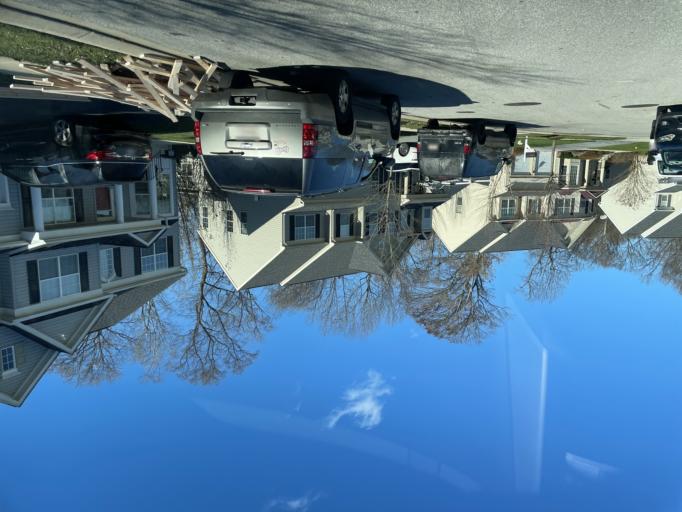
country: US
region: Maryland
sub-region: Baltimore County
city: Pikesville
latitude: 39.3704
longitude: -76.6689
